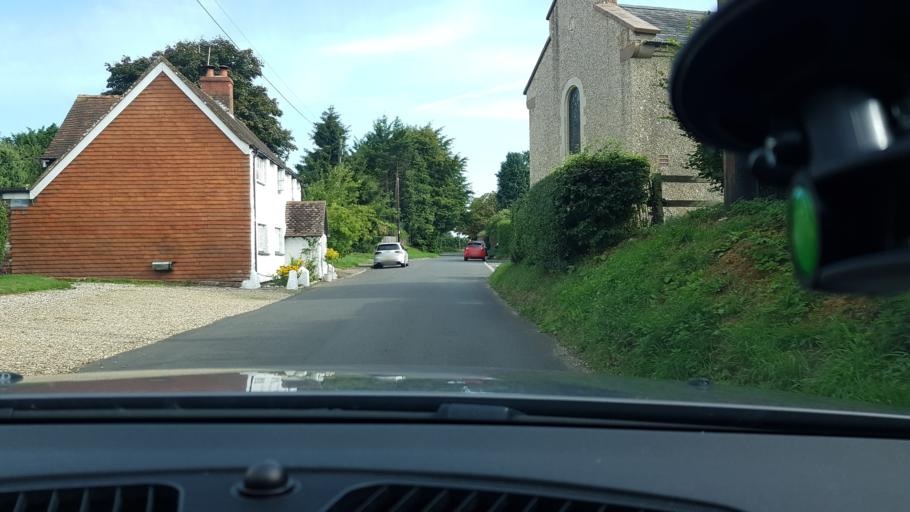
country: GB
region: England
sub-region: West Berkshire
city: Wickham
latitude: 51.4559
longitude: -1.4751
